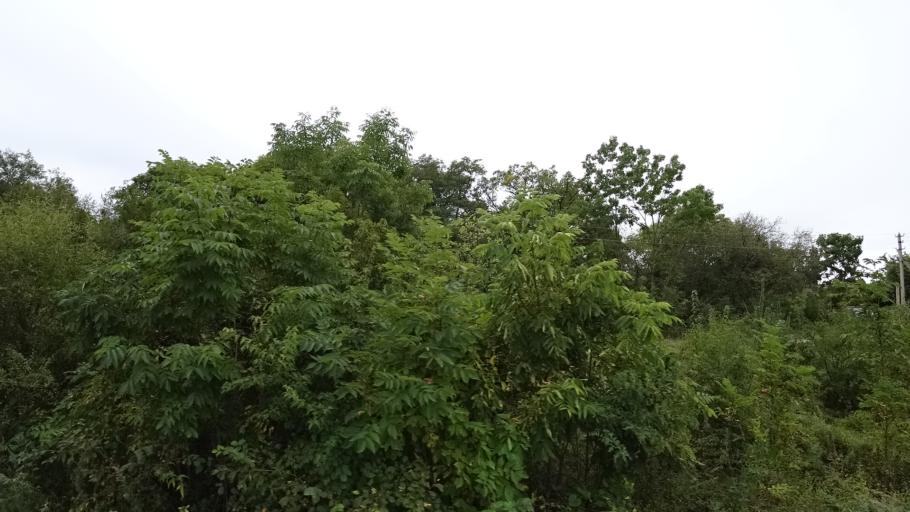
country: RU
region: Primorskiy
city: Monastyrishche
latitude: 44.0817
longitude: 132.5913
